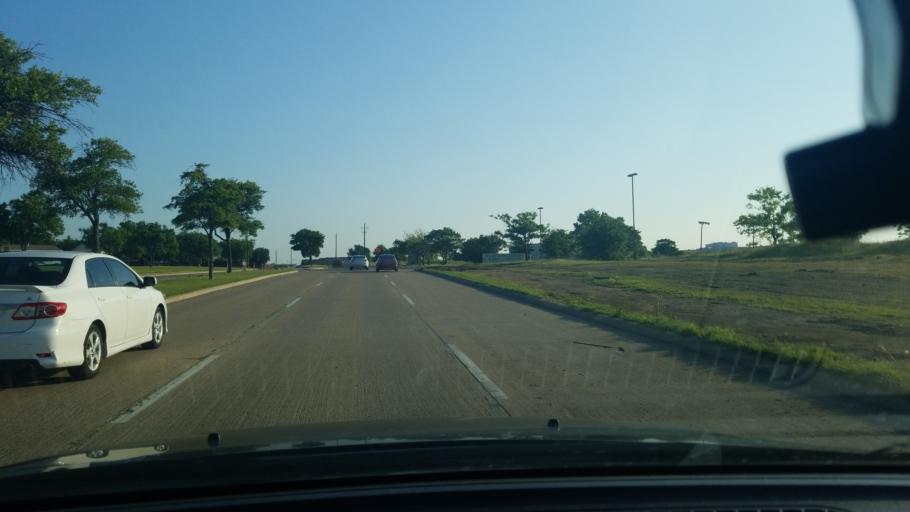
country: US
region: Texas
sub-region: Dallas County
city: Mesquite
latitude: 32.8029
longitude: -96.6335
